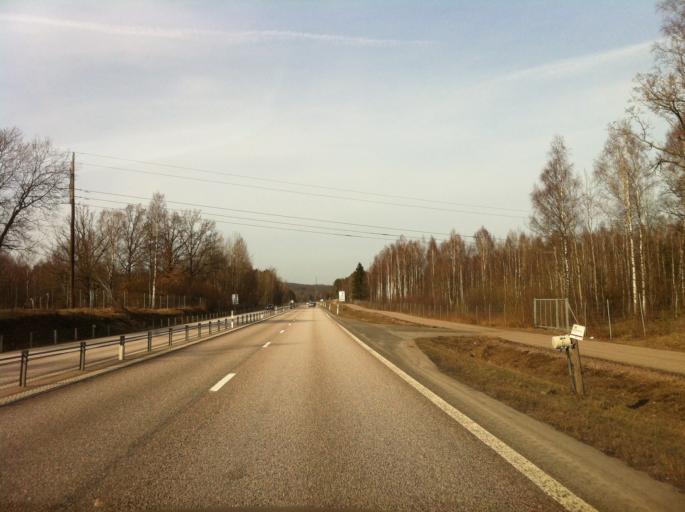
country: SE
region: Vaestra Goetaland
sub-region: Skovde Kommun
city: Stopen
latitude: 58.4366
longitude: 13.8582
